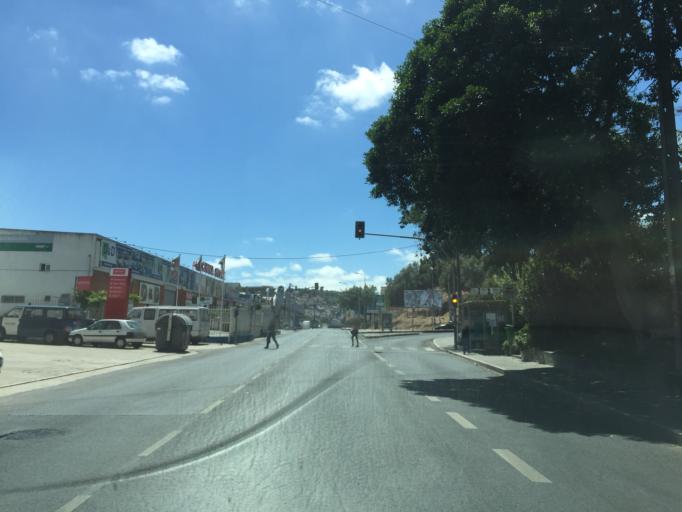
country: PT
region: Lisbon
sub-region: Odivelas
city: Povoa de Santo Adriao
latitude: 38.8071
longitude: -9.1575
